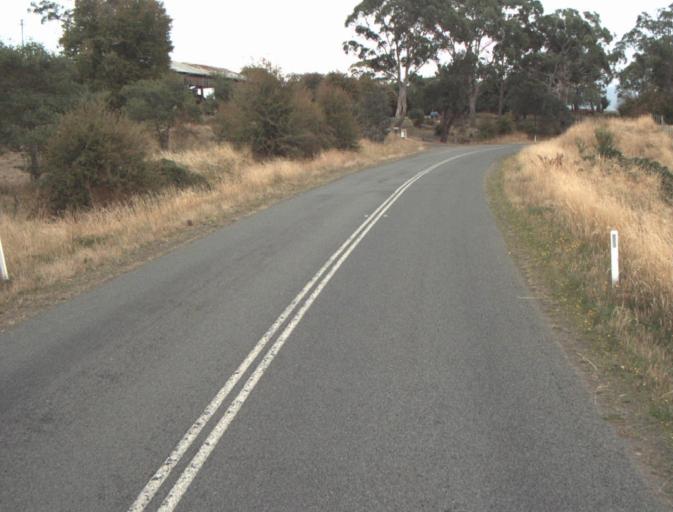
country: AU
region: Tasmania
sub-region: Northern Midlands
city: Evandale
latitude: -41.5026
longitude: 147.4754
